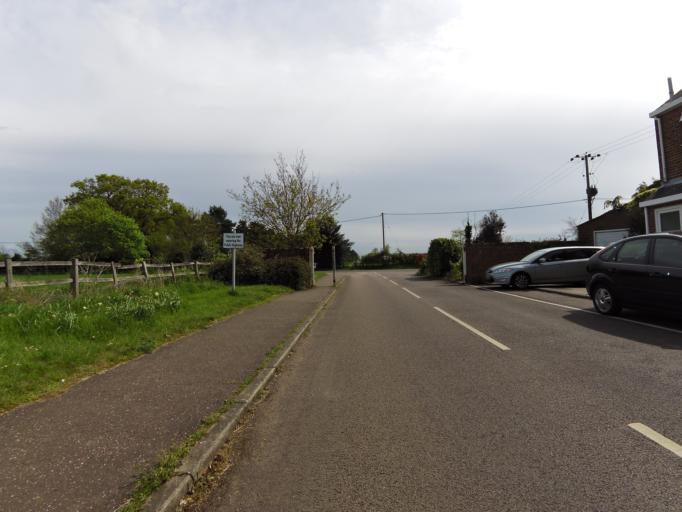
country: GB
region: England
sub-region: Essex
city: Mistley
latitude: 51.9710
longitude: 1.1379
